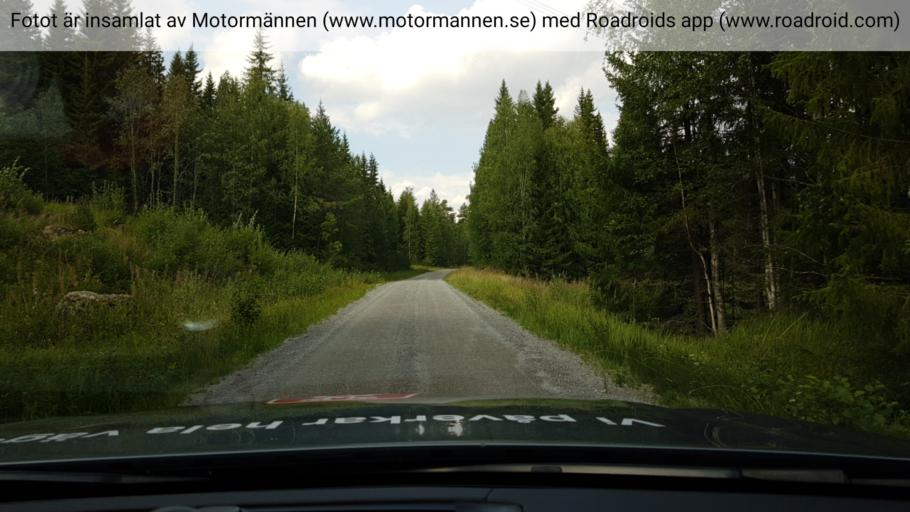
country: SE
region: Jaemtland
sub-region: OEstersunds Kommun
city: Brunflo
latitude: 63.0287
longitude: 15.0702
